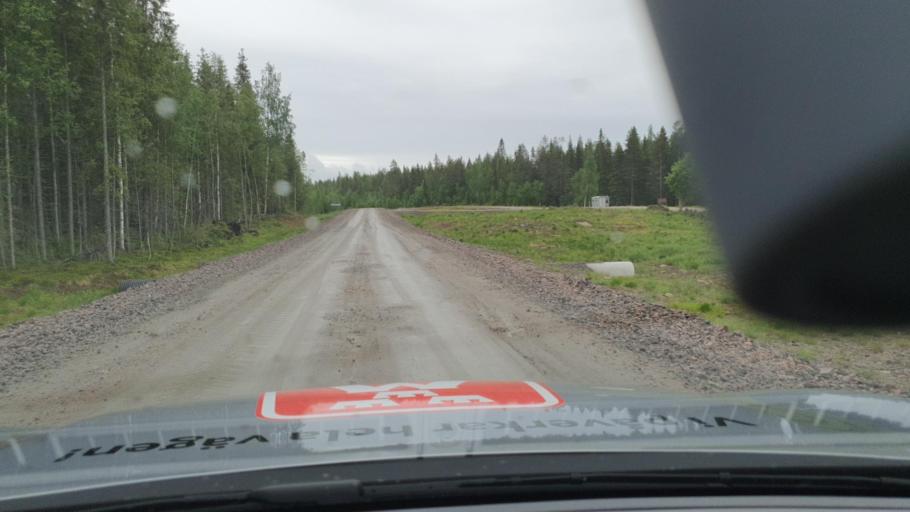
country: SE
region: Norrbotten
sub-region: Overtornea Kommun
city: OEvertornea
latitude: 66.4525
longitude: 23.4850
